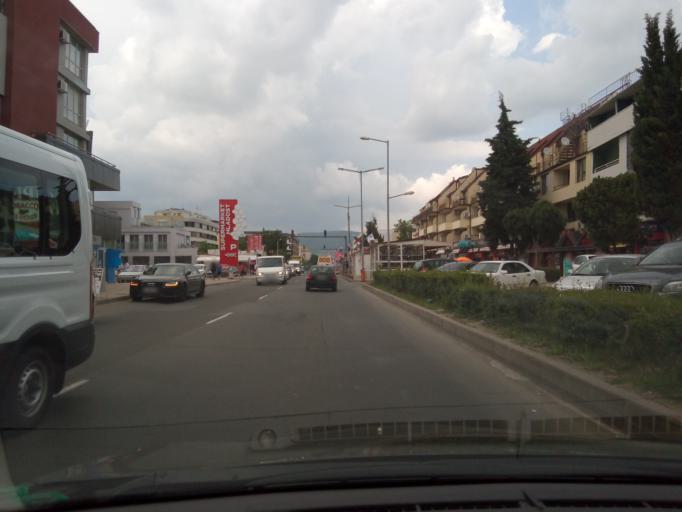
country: BG
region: Burgas
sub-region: Obshtina Nesebur
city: Nesebar
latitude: 42.6942
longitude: 27.7097
